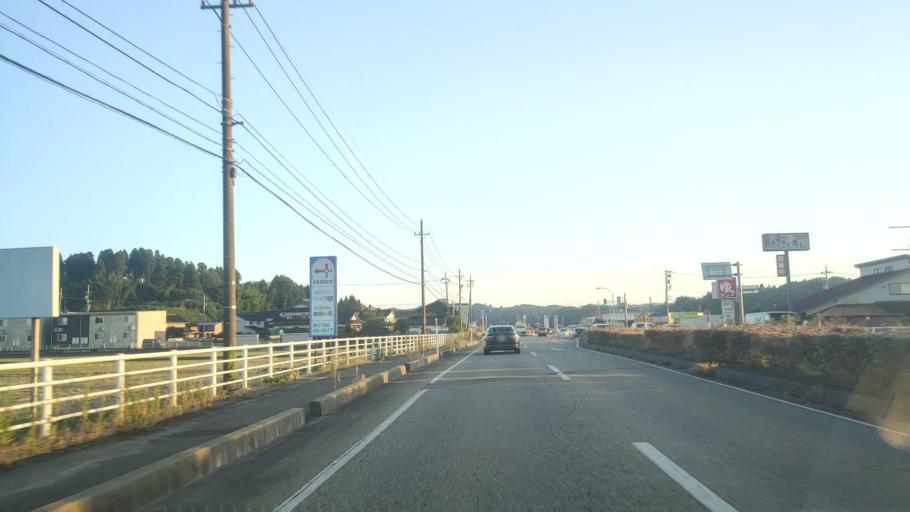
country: JP
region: Toyama
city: Himi
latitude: 36.8220
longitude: 136.9950
